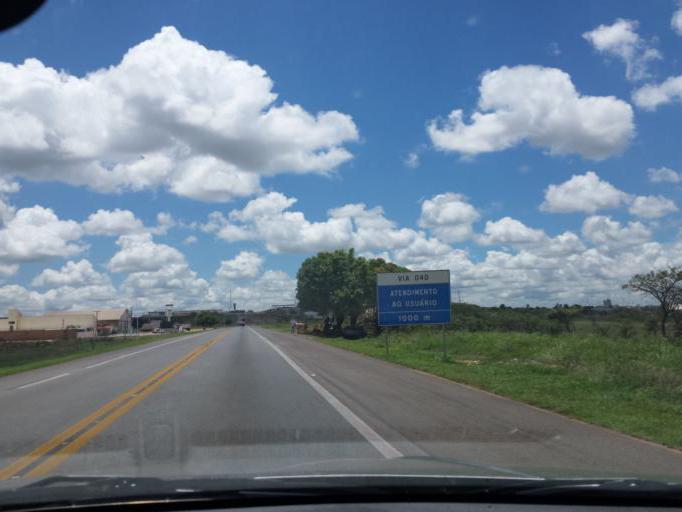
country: BR
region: Goias
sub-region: Cristalina
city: Cristalina
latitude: -16.7425
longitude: -47.6144
